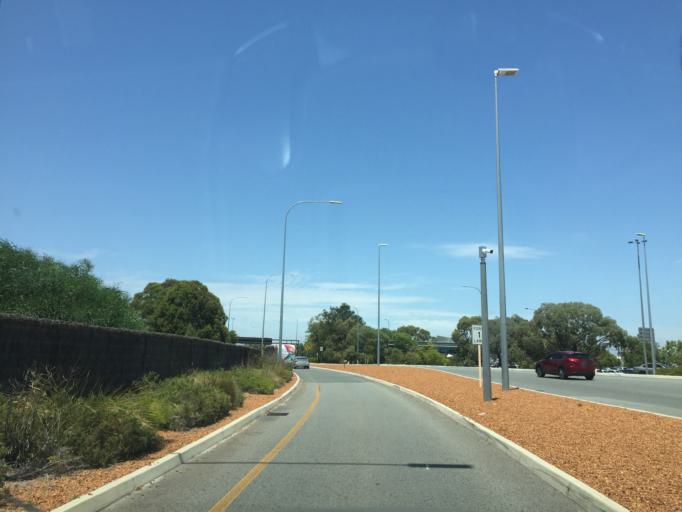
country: AU
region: Western Australia
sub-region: Belmont
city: Redcliffe
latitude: -31.9454
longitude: 115.9748
